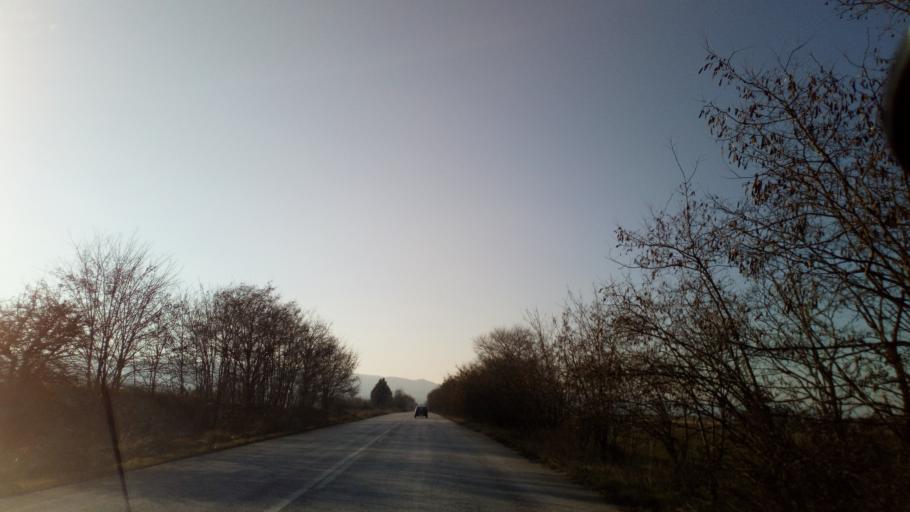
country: GR
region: Central Macedonia
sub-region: Nomos Thessalonikis
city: Agios Vasileios
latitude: 40.6565
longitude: 23.1514
